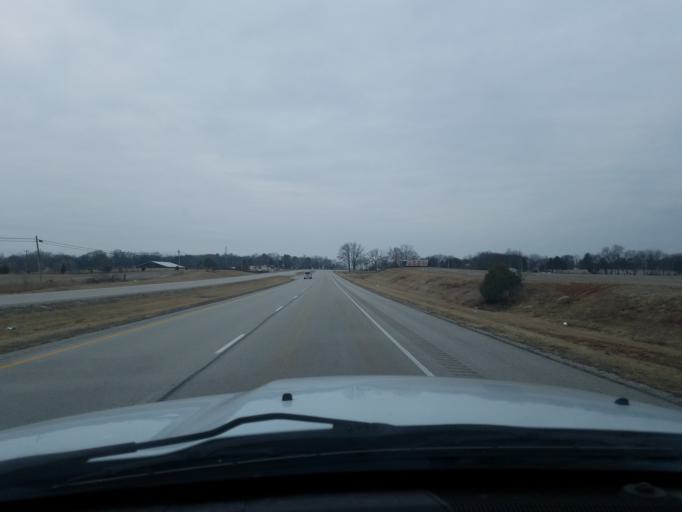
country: US
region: Kentucky
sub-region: Warren County
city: Bowling Green
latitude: 36.9175
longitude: -86.5635
